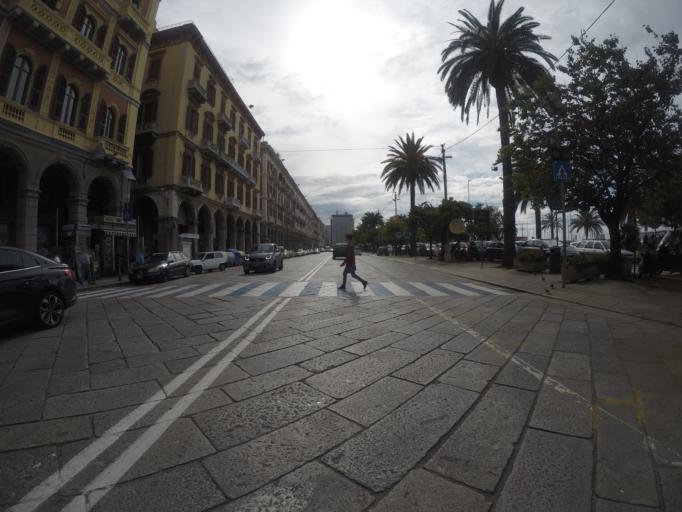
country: IT
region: Sardinia
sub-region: Provincia di Cagliari
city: Cagliari
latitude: 39.2142
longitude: 9.1120
